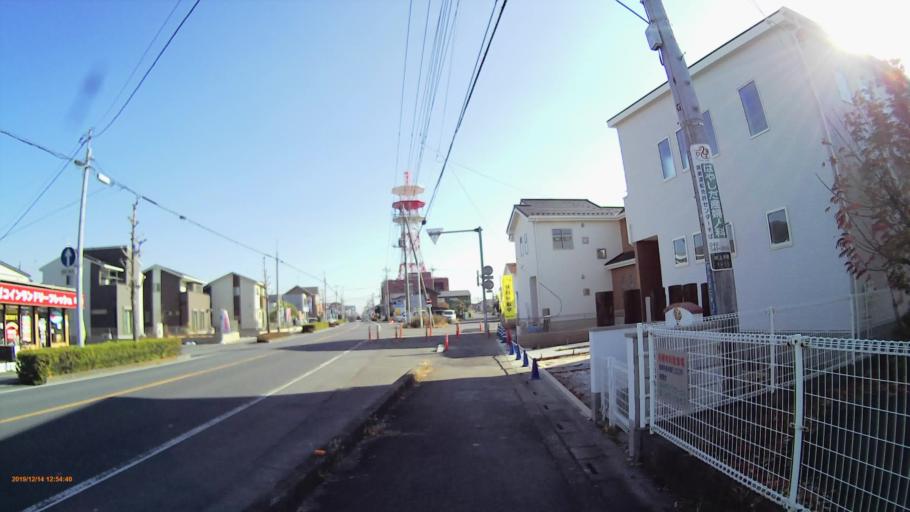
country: JP
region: Saitama
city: Fukiage-fujimi
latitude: 36.1024
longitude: 139.4572
